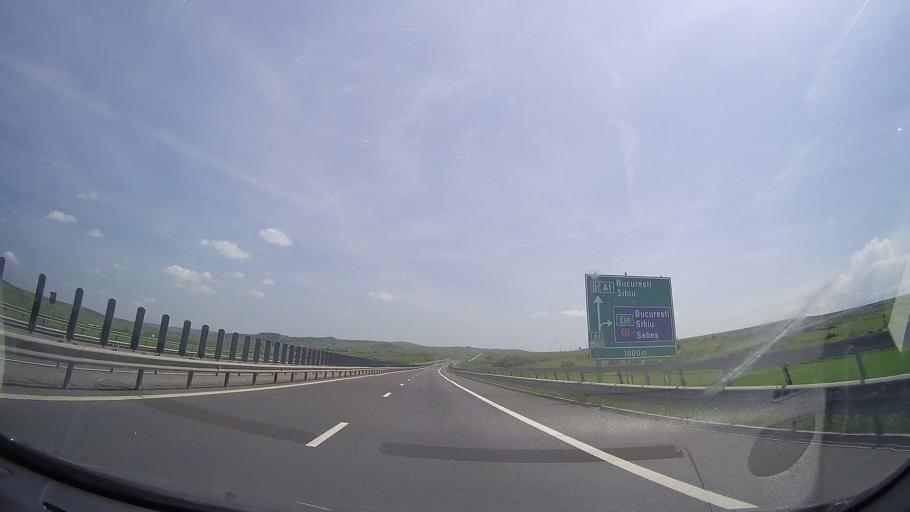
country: RO
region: Alba
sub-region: Comuna Cut
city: Cut
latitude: 45.9225
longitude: 23.7055
